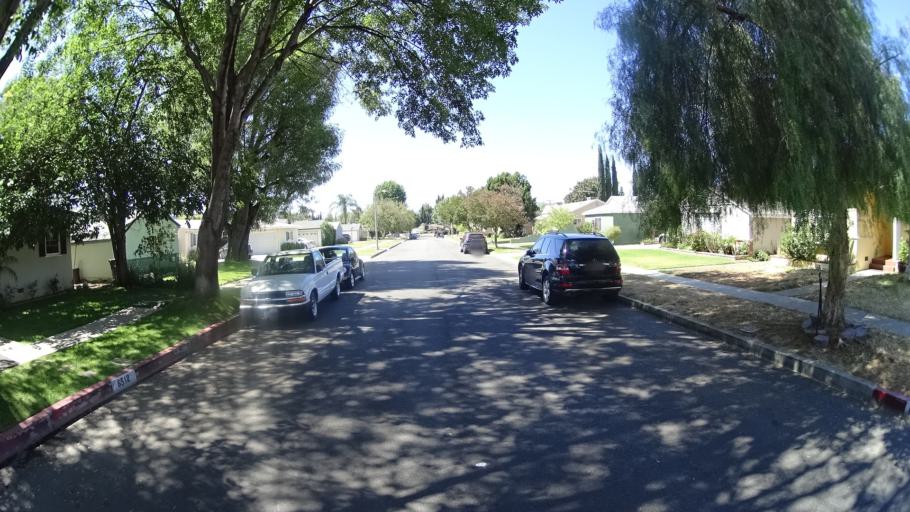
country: US
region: California
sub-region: Los Angeles County
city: Van Nuys
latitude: 34.1893
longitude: -118.5001
